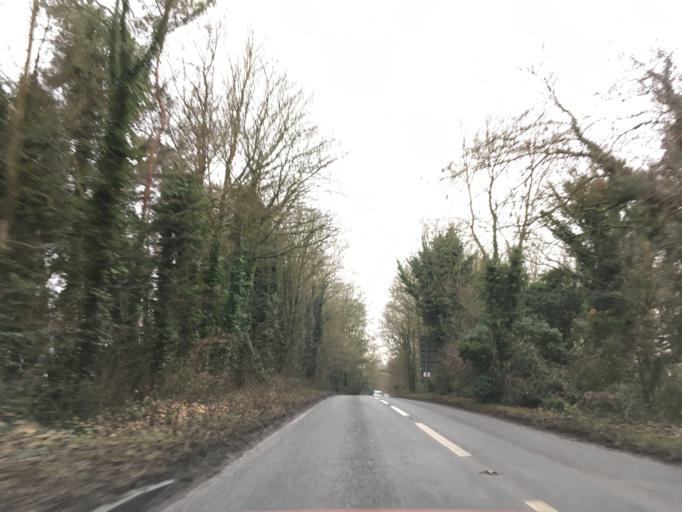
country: GB
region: England
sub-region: Gloucestershire
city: Coates
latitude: 51.7006
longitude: -2.0016
